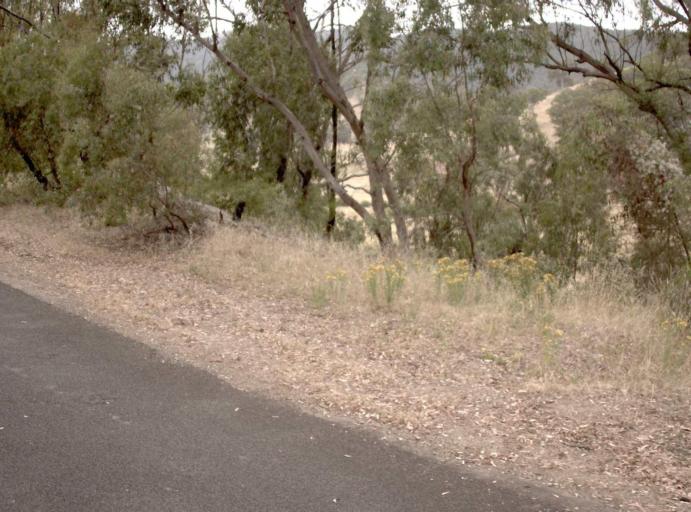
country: AU
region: Victoria
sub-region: Wellington
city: Heyfield
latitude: -37.6931
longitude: 146.6502
